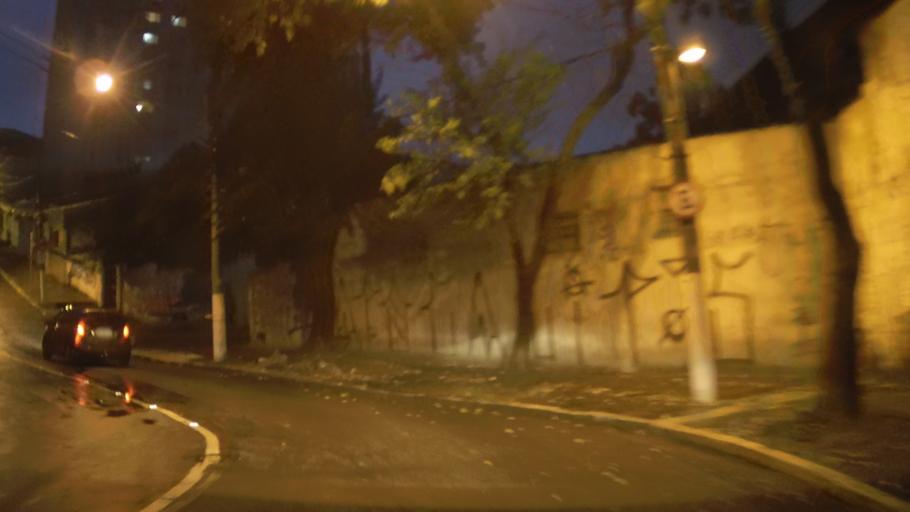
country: BR
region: Sao Paulo
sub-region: Sao Paulo
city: Sao Paulo
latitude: -23.5899
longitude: -46.6145
